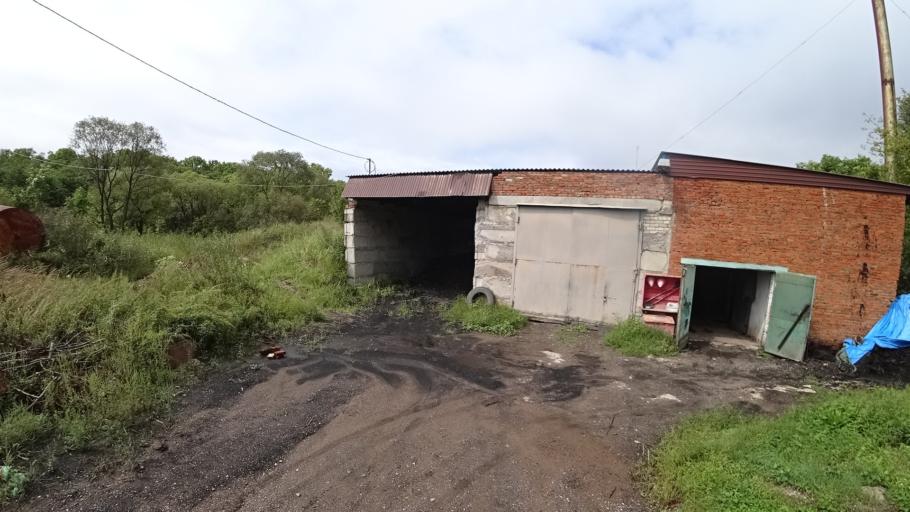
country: RU
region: Primorskiy
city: Monastyrishche
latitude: 44.1681
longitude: 132.5380
